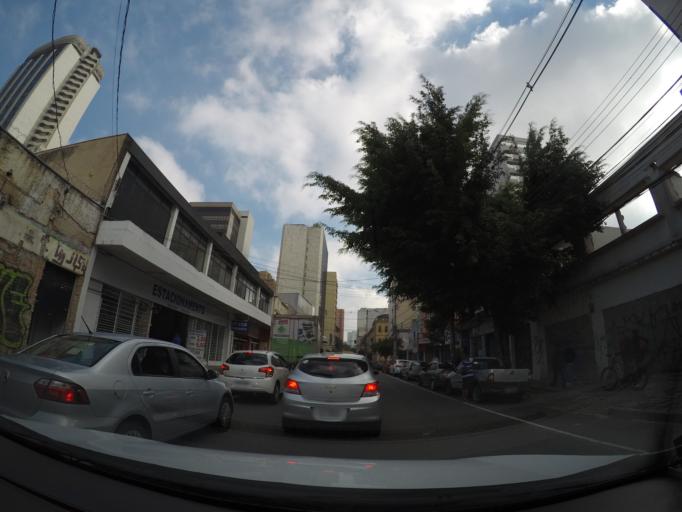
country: BR
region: Parana
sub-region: Curitiba
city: Curitiba
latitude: -25.4303
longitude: -49.2649
